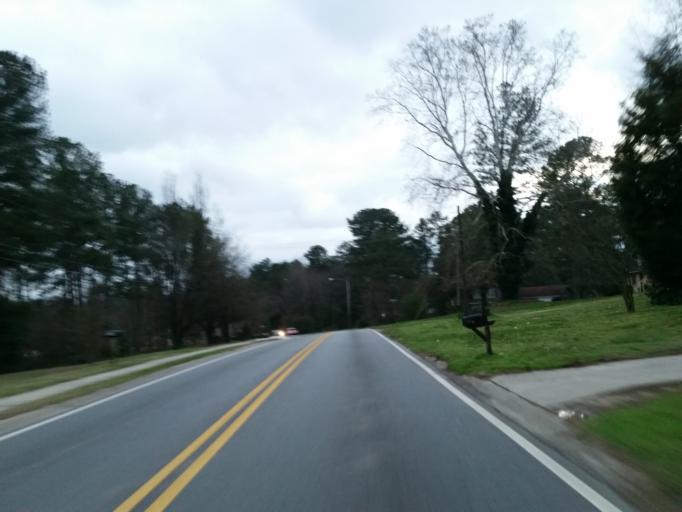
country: US
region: Georgia
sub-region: Cobb County
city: Fair Oaks
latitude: 33.8753
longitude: -84.5798
